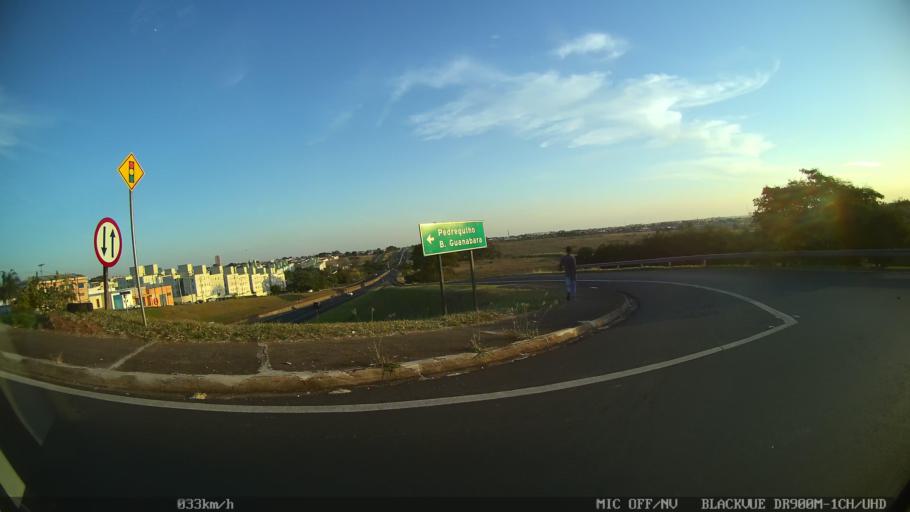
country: BR
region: Sao Paulo
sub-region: Franca
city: Franca
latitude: -20.5145
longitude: -47.4154
